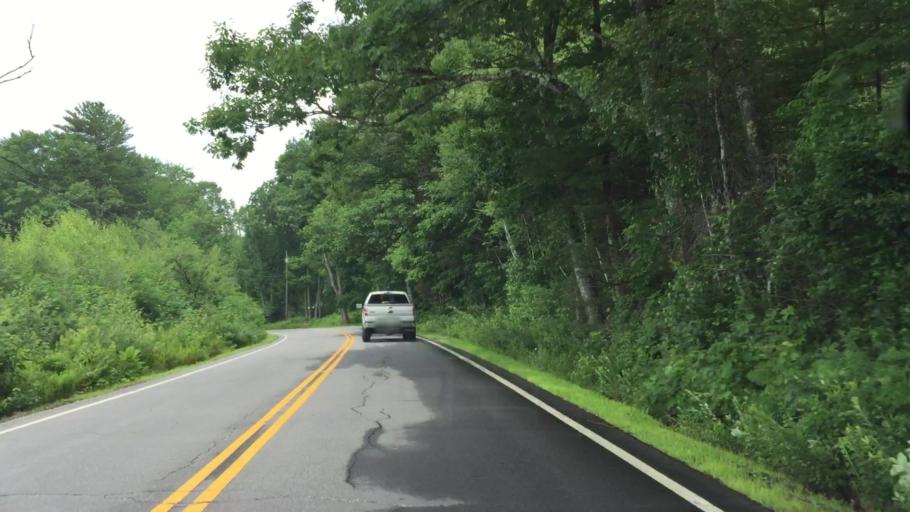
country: US
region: New Hampshire
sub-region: Carroll County
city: Sandwich
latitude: 43.8055
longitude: -71.4587
